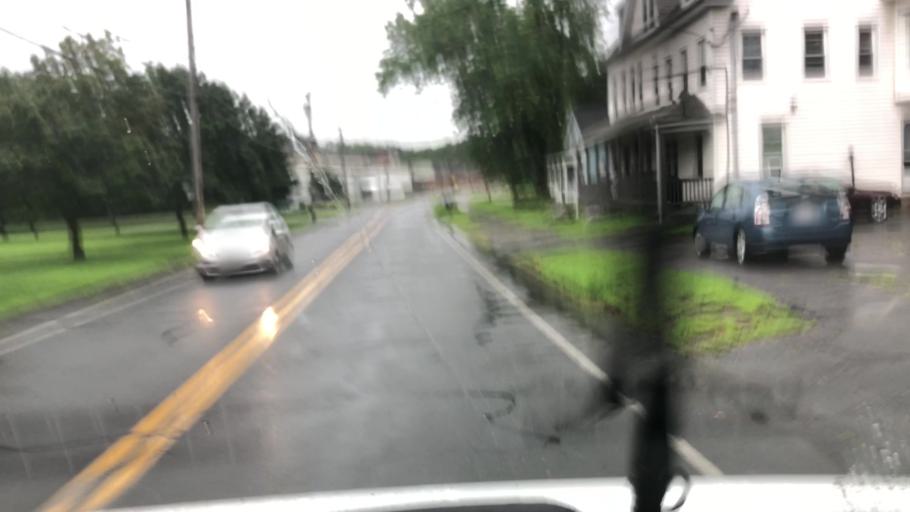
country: US
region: Massachusetts
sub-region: Hampshire County
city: Northampton
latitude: 42.3307
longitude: -72.6726
